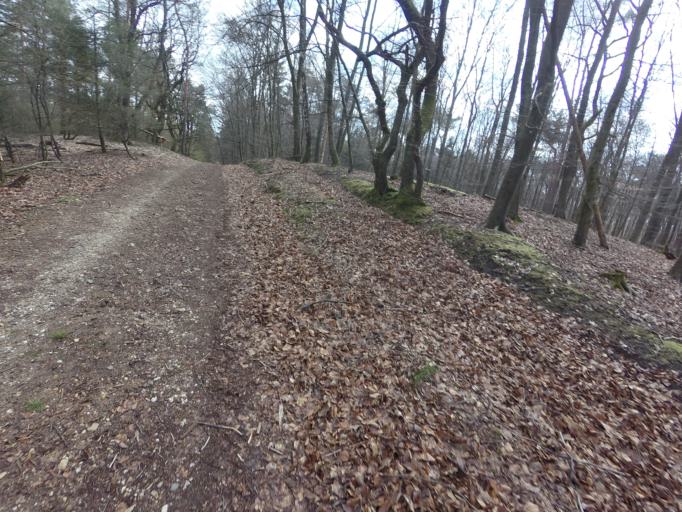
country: NL
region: Limburg
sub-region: Gemeente Roerdalen
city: Herkenbosch
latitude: 51.1765
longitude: 6.0968
